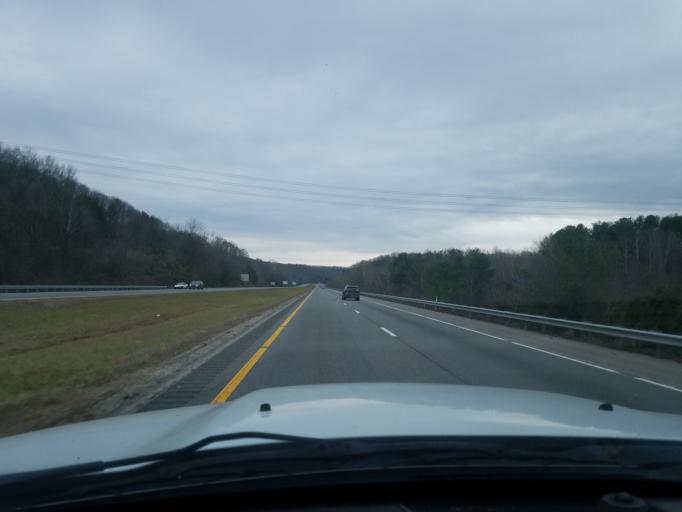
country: US
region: Kentucky
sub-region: Boyd County
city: Meads
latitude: 38.3647
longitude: -82.7163
